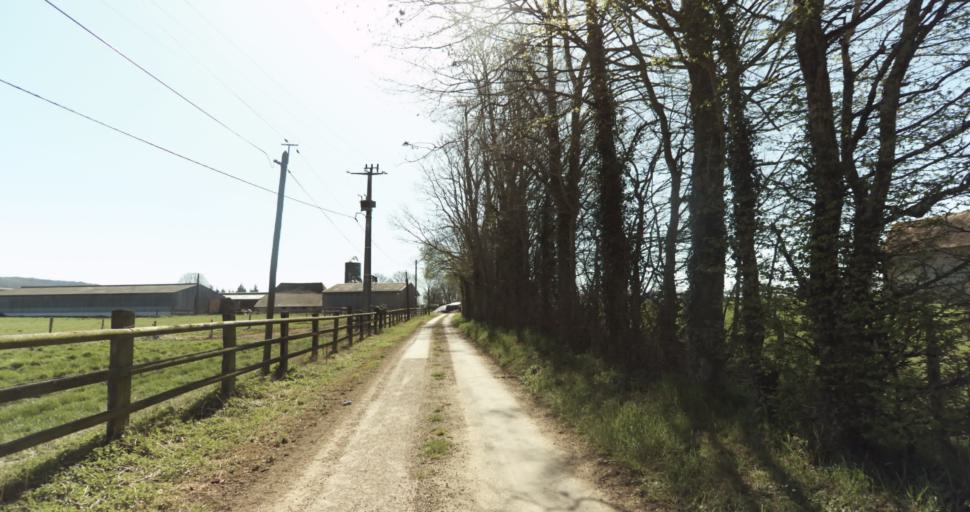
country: FR
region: Lower Normandy
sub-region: Departement du Calvados
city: Saint-Pierre-sur-Dives
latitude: 49.0012
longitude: 0.0256
